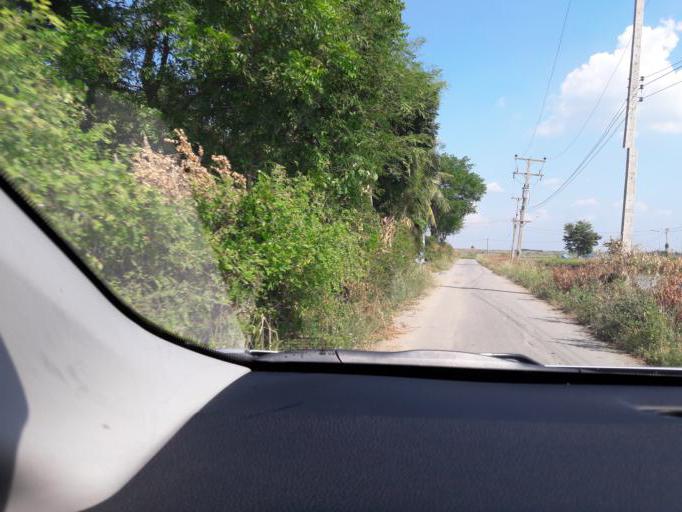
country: TH
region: Ang Thong
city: Wiset Chaichan
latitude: 14.5584
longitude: 100.3905
